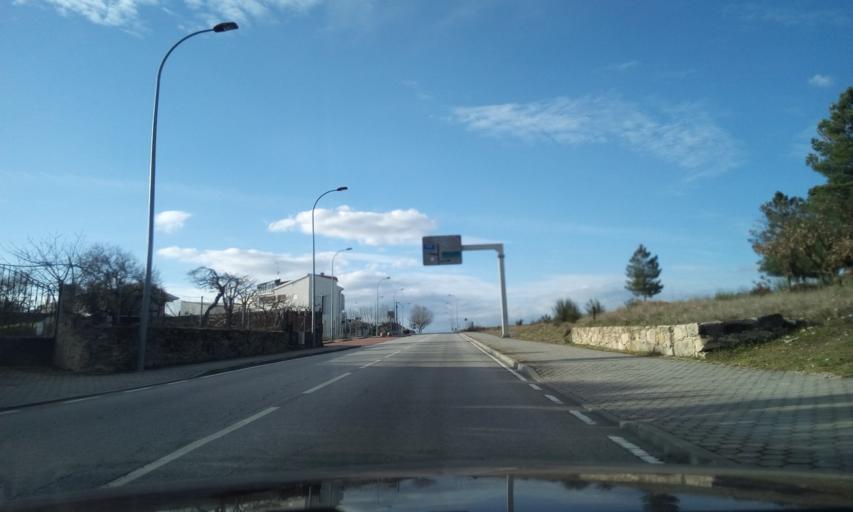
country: ES
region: Castille and Leon
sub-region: Provincia de Salamanca
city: Fuentes de Onoro
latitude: 40.6162
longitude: -6.8403
